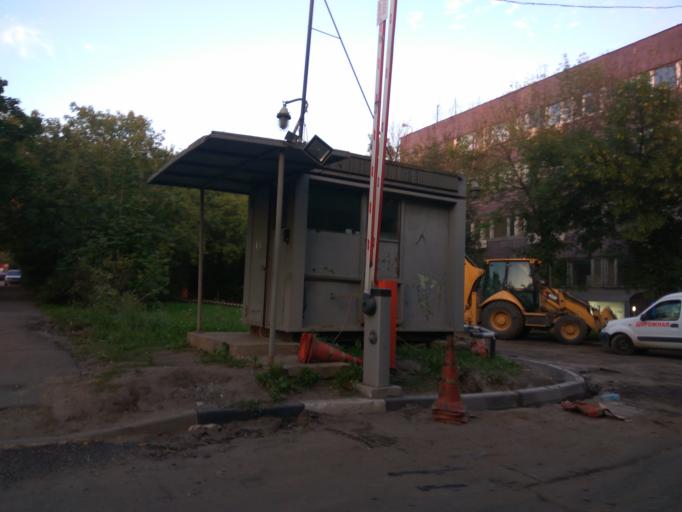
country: RU
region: Moscow
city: Mar'ino
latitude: 55.6572
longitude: 37.7296
